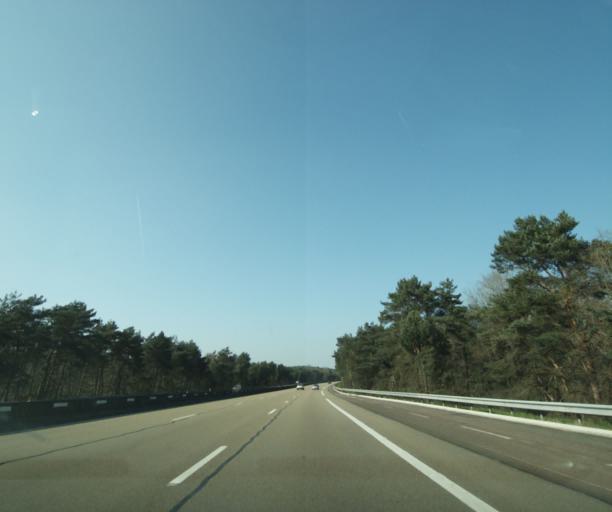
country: FR
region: Ile-de-France
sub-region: Departement de Seine-et-Marne
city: Arbonne-la-Foret
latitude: 48.3905
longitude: 2.5551
